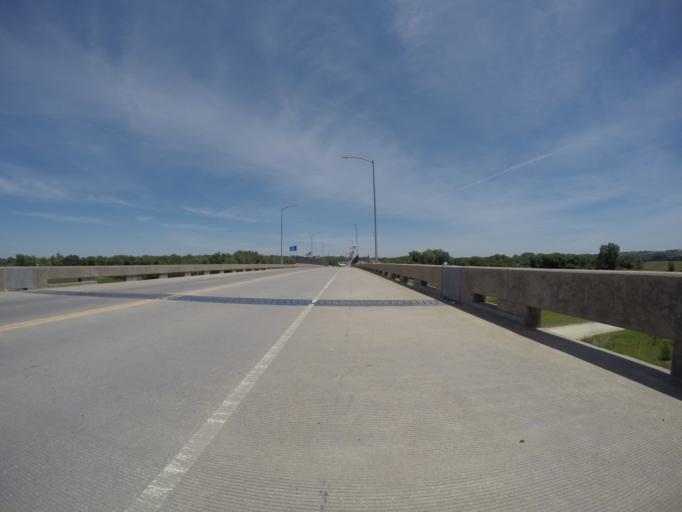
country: US
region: Kansas
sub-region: Marshall County
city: Marysville
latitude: 39.8421
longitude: -96.6585
